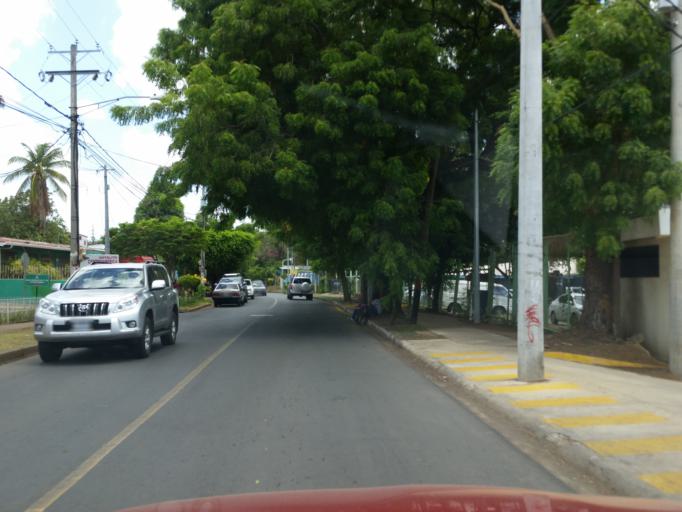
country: NI
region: Managua
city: Managua
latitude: 12.1152
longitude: -86.2501
